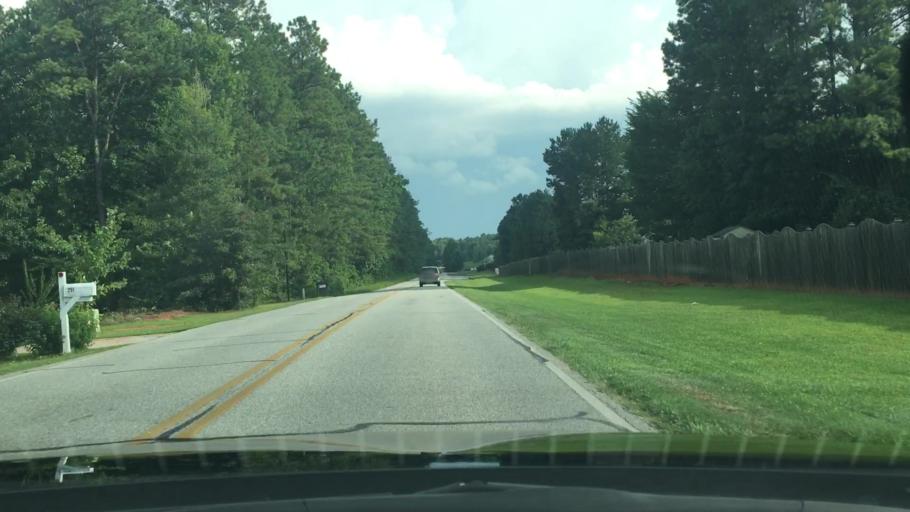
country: US
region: Georgia
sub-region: Coweta County
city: East Newnan
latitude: 33.3812
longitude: -84.7028
